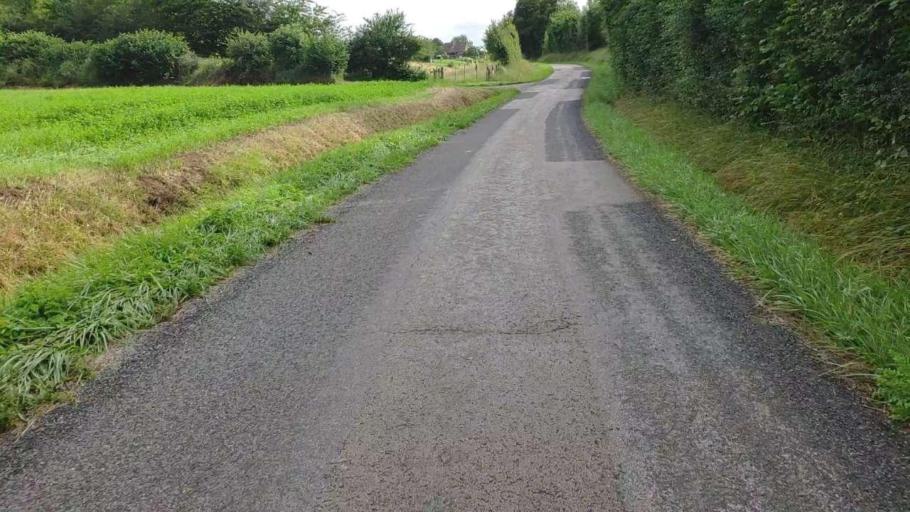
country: FR
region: Franche-Comte
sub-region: Departement du Jura
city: Poligny
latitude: 46.8277
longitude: 5.5807
